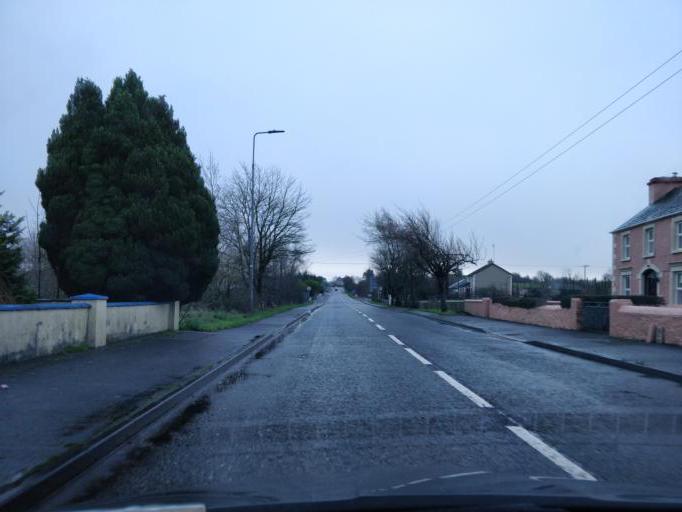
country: IE
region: Connaught
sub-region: Maigh Eo
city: Ballyhaunis
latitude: 53.7609
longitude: -8.7537
